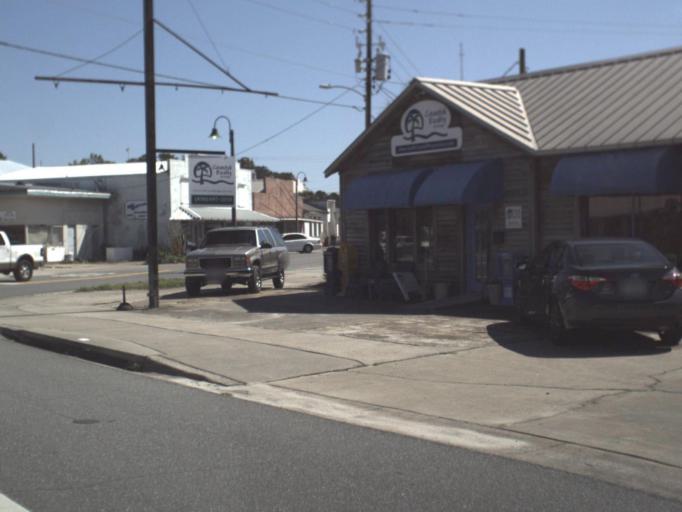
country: US
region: Florida
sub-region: Franklin County
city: Carrabelle
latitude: 29.8512
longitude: -84.6650
